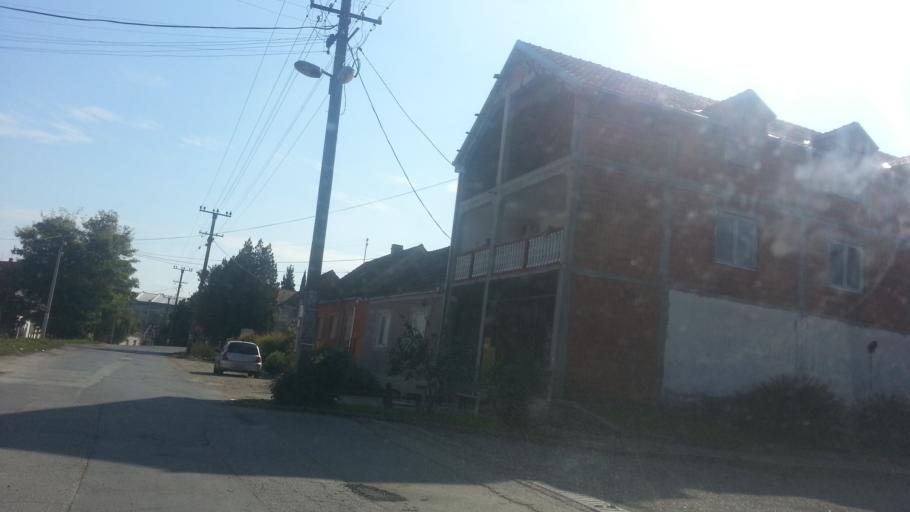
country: RS
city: Novi Slankamen
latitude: 45.1421
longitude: 20.2580
